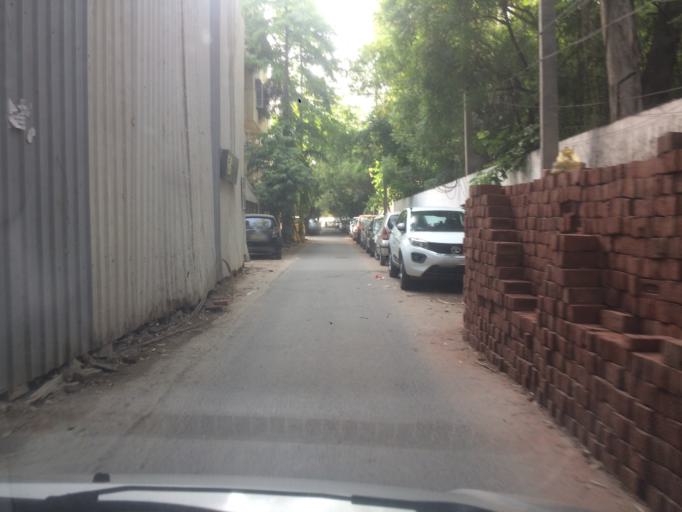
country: IN
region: NCT
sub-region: New Delhi
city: New Delhi
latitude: 28.5472
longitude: 77.2323
